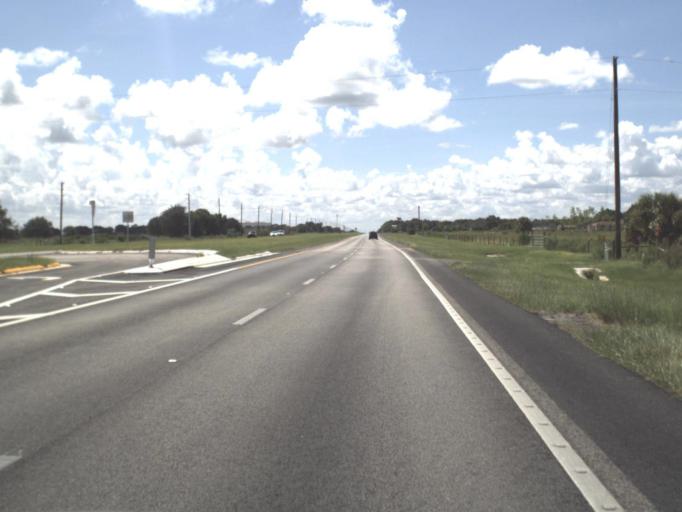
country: US
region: Florida
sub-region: Charlotte County
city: Harbour Heights
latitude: 27.0630
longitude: -81.9584
